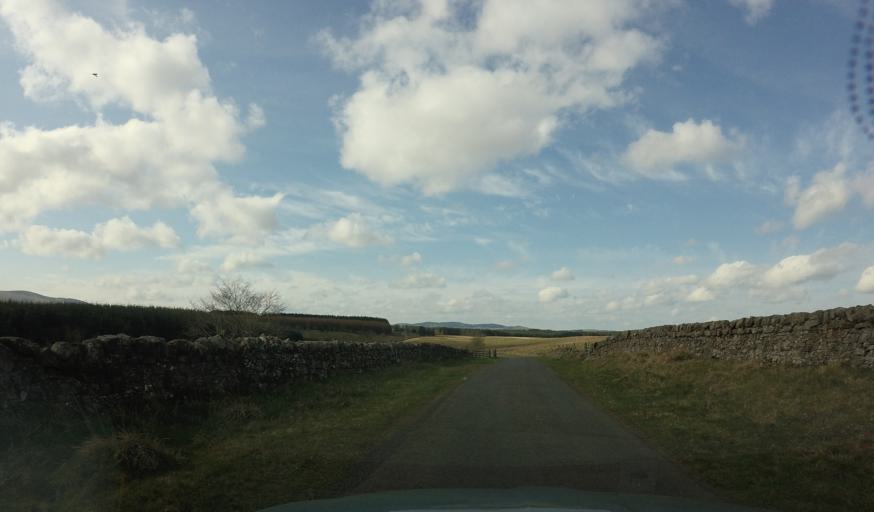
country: GB
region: Scotland
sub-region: Midlothian
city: Penicuik
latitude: 55.7880
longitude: -3.1694
